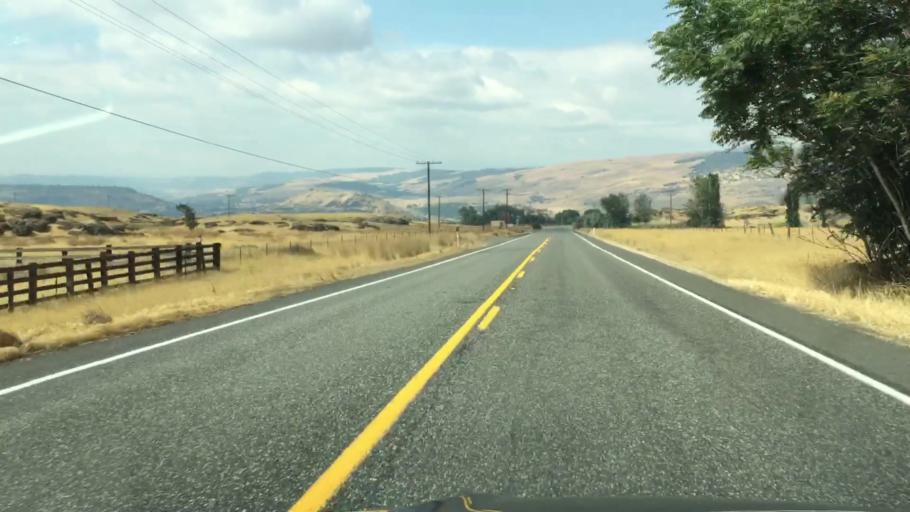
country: US
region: Washington
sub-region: Klickitat County
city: Dallesport
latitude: 45.6486
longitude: -121.1699
